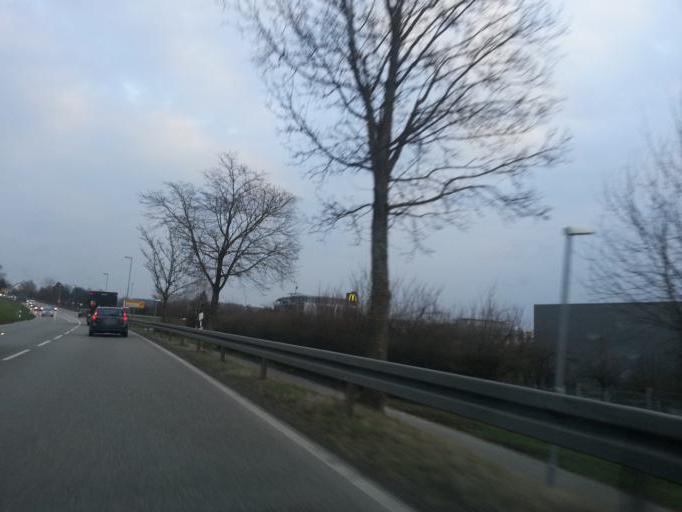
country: DE
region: Baden-Wuerttemberg
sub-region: Tuebingen Region
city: Markdorf
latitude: 47.7173
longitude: 9.4006
